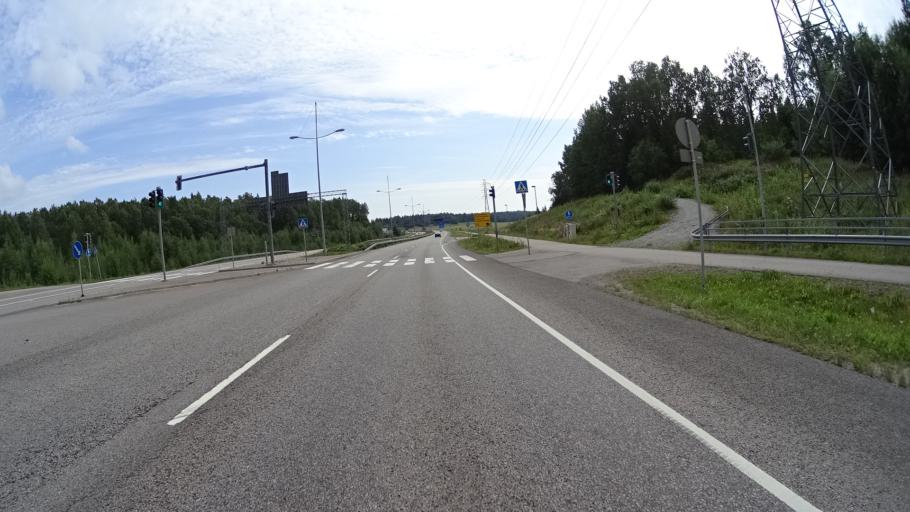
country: FI
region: Uusimaa
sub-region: Helsinki
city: Vantaa
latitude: 60.2547
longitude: 25.1301
